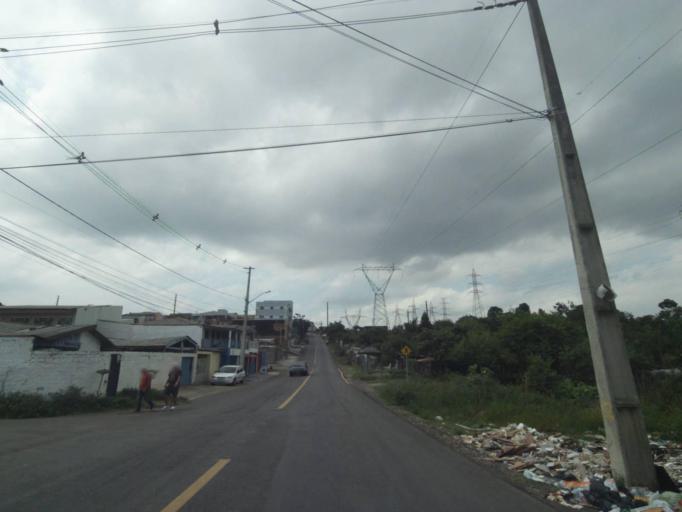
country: BR
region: Parana
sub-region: Curitiba
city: Curitiba
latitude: -25.5028
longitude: -49.3429
